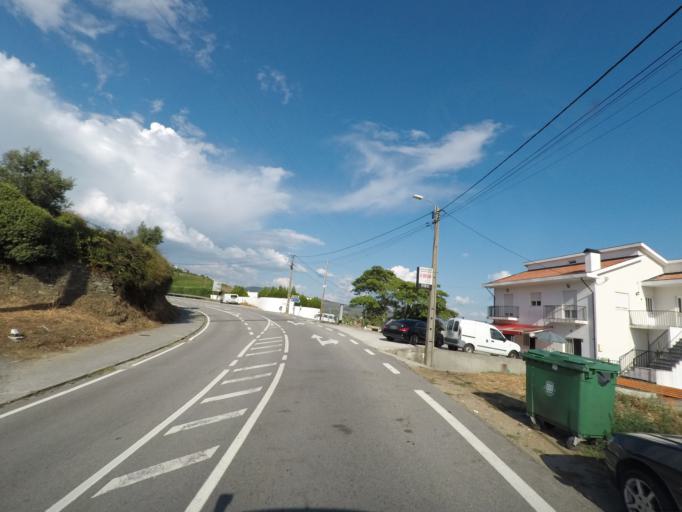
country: PT
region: Vila Real
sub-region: Mesao Frio
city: Mesao Frio
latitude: 41.1595
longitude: -7.8872
